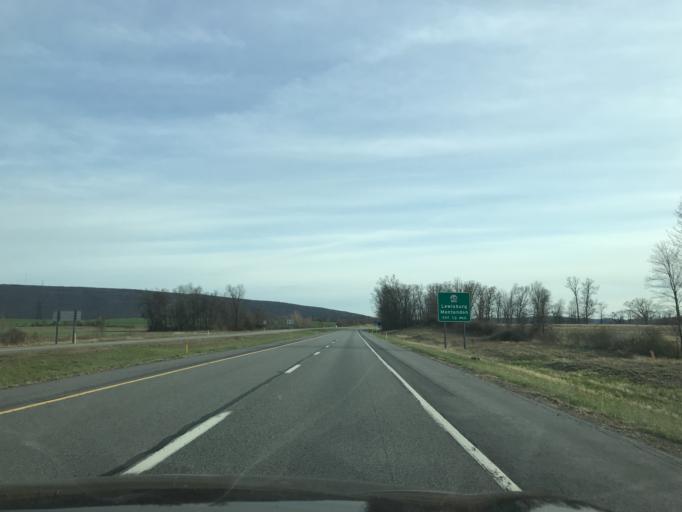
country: US
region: Pennsylvania
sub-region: Northumberland County
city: Milton
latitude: 40.9765
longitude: -76.8396
